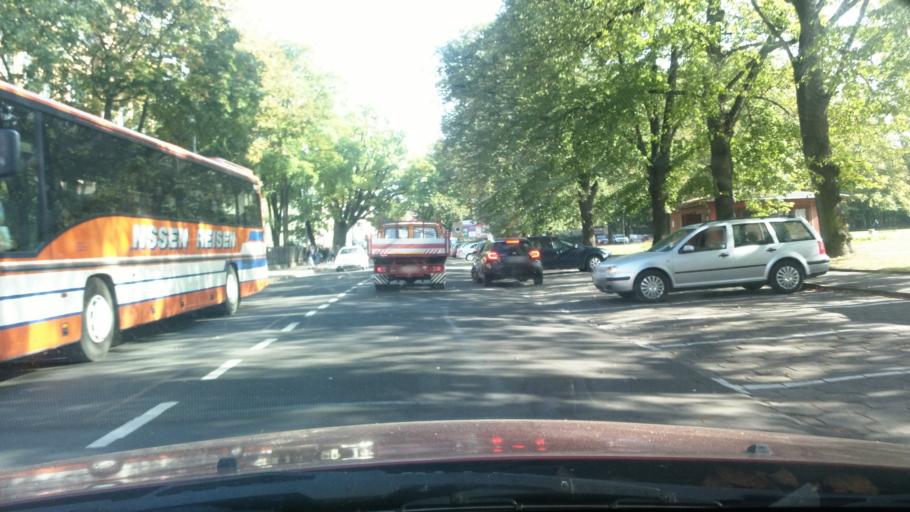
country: PL
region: Lower Silesian Voivodeship
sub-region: Powiat zgorzelecki
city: Zgorzelec
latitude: 51.1487
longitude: 15.0040
